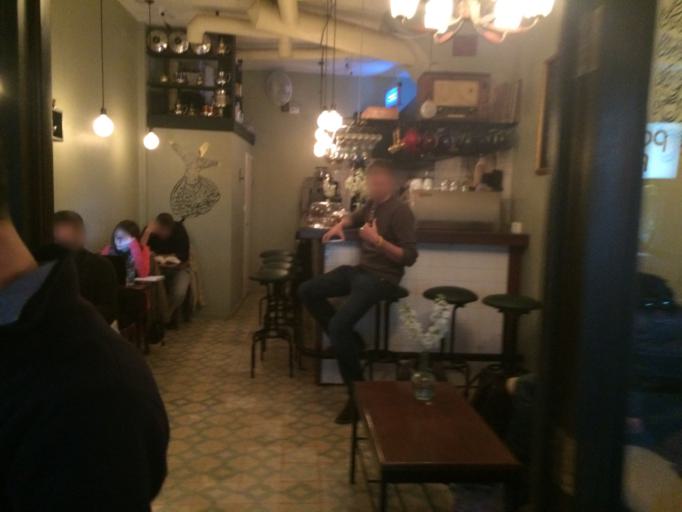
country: JO
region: Amman
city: Amman
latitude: 31.9561
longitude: 35.9258
